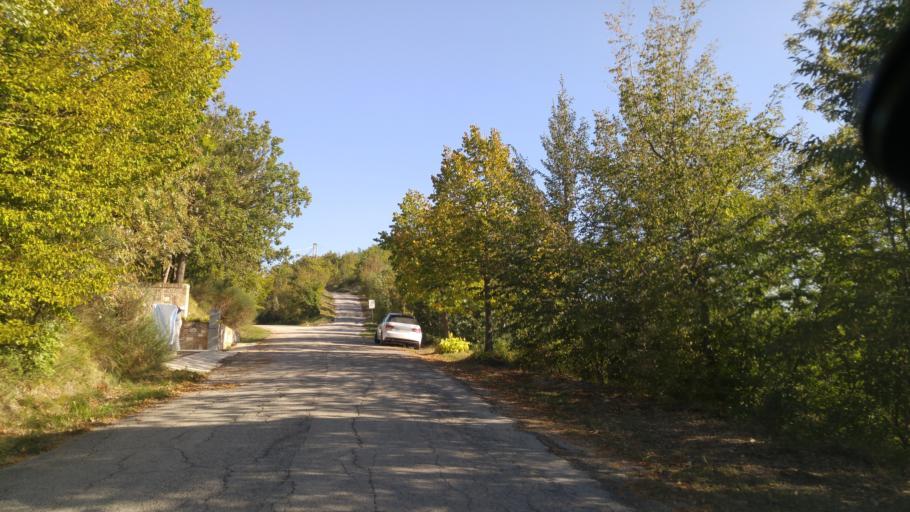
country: IT
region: The Marches
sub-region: Provincia di Pesaro e Urbino
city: Fermignano
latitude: 43.6580
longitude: 12.6459
